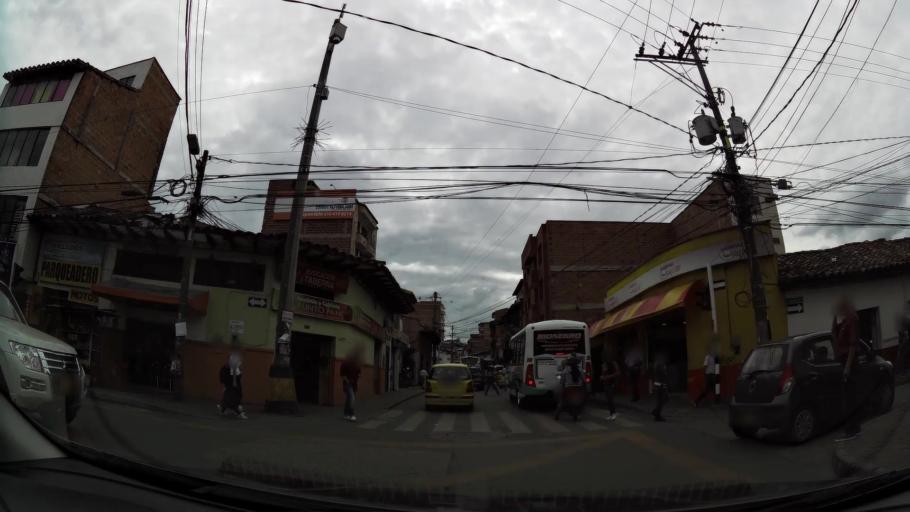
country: CO
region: Antioquia
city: Rionegro
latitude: 6.1521
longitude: -75.3738
